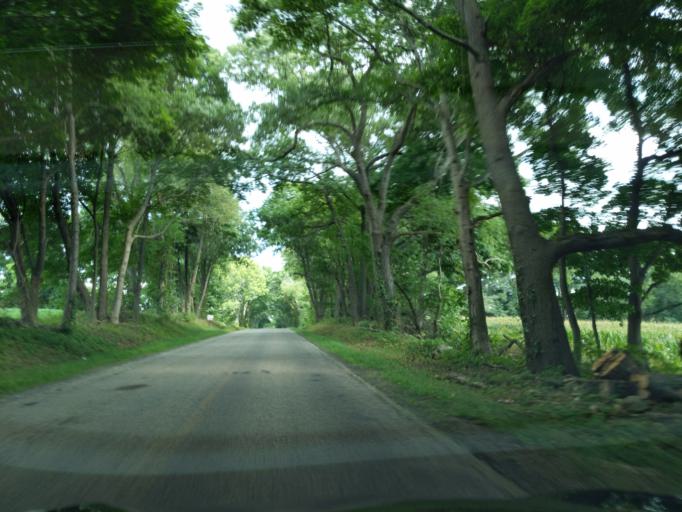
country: US
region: Michigan
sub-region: Eaton County
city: Eaton Rapids
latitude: 42.3787
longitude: -84.5822
